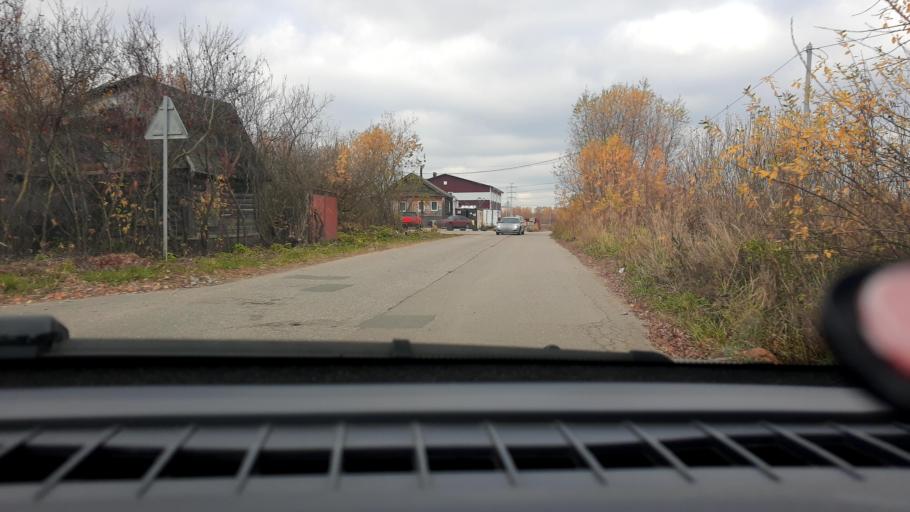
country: RU
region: Nizjnij Novgorod
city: Afonino
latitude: 56.2004
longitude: 44.0956
